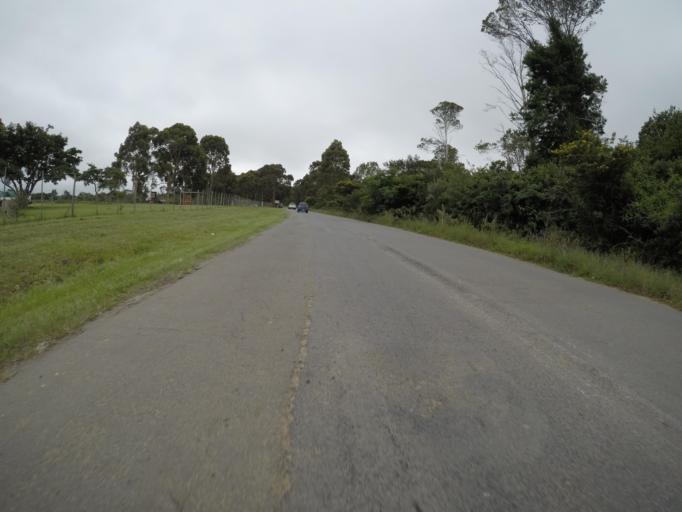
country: ZA
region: Eastern Cape
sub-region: Buffalo City Metropolitan Municipality
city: East London
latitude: -32.9384
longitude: 27.9414
